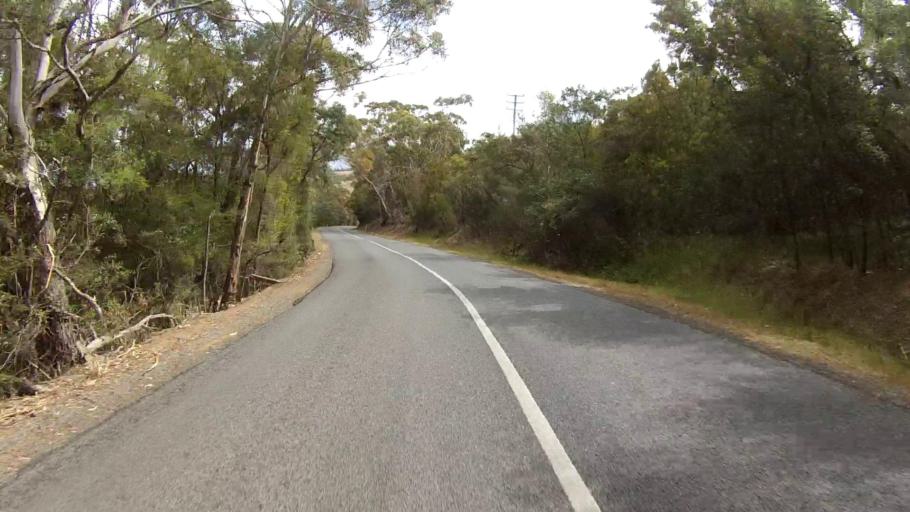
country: AU
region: Tasmania
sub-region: Clarence
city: Howrah
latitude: -42.8567
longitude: 147.4197
